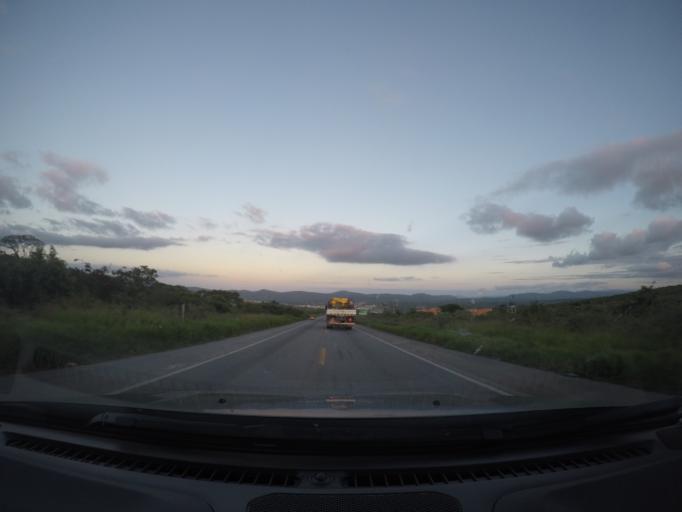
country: BR
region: Bahia
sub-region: Seabra
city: Seabra
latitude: -12.4321
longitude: -41.8060
